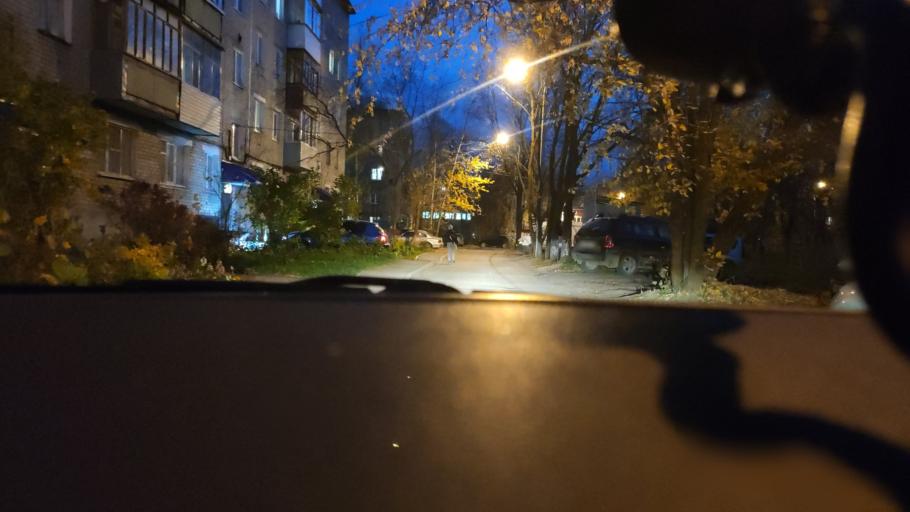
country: RU
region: Perm
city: Perm
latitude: 57.9833
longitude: 56.2882
